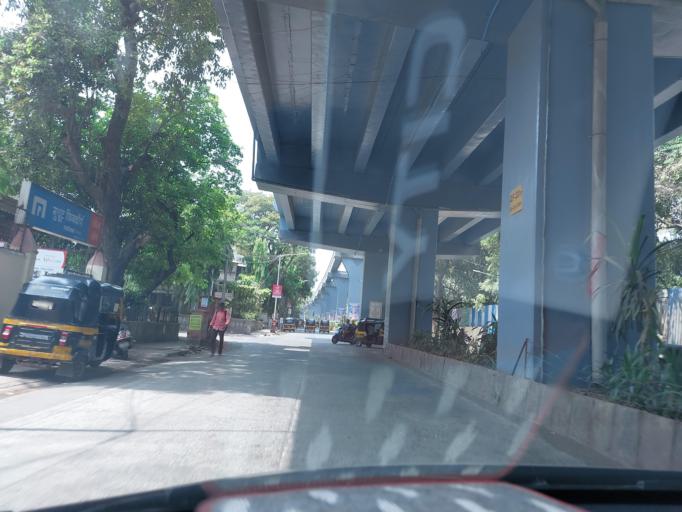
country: IN
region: Maharashtra
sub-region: Mumbai Suburban
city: Mumbai
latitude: 19.0598
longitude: 72.8967
